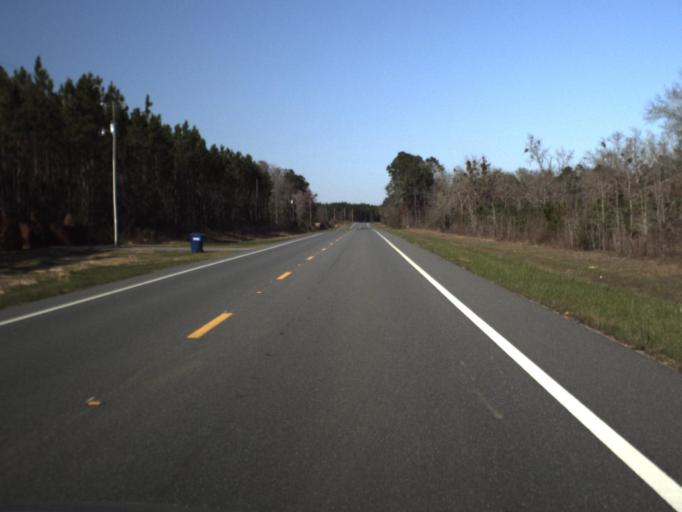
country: US
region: Florida
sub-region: Calhoun County
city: Blountstown
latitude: 30.4054
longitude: -85.2110
